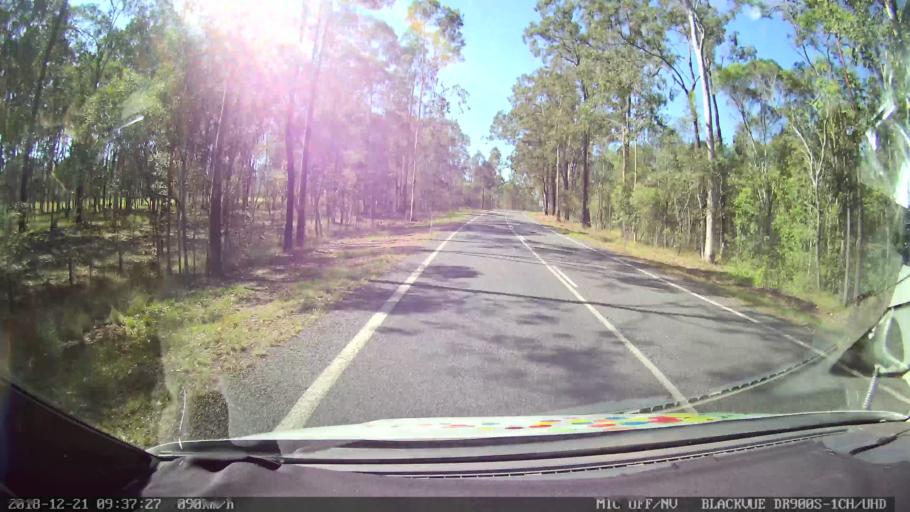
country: AU
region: New South Wales
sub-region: Clarence Valley
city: Grafton
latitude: -29.5365
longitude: 152.9866
